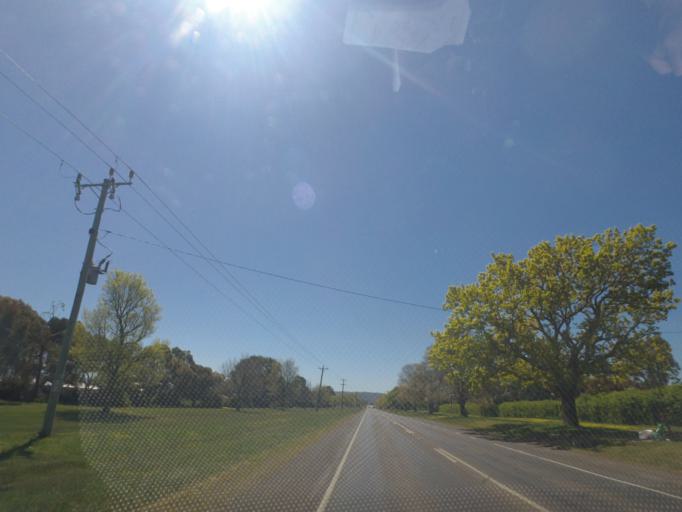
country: AU
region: Victoria
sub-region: Hume
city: Sunbury
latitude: -37.2849
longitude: 144.7367
